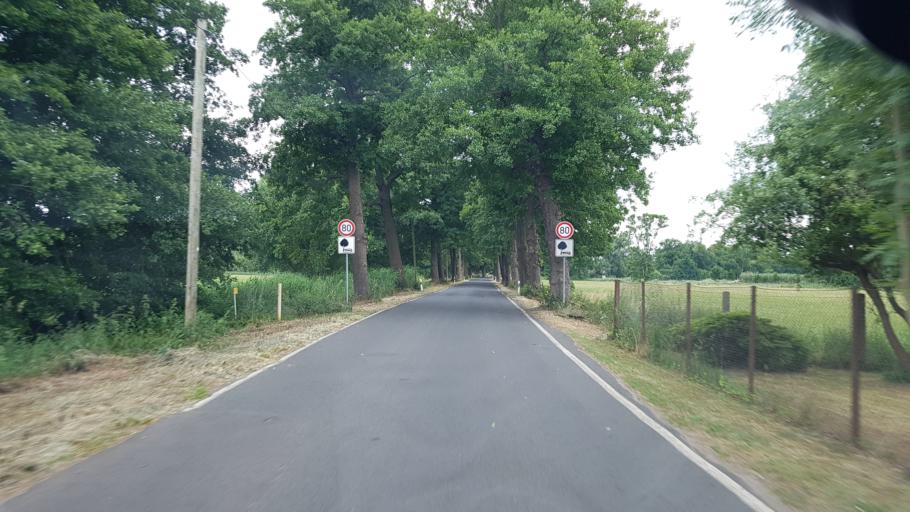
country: DE
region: Brandenburg
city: Kasel-Golzig
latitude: 51.9829
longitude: 13.6924
